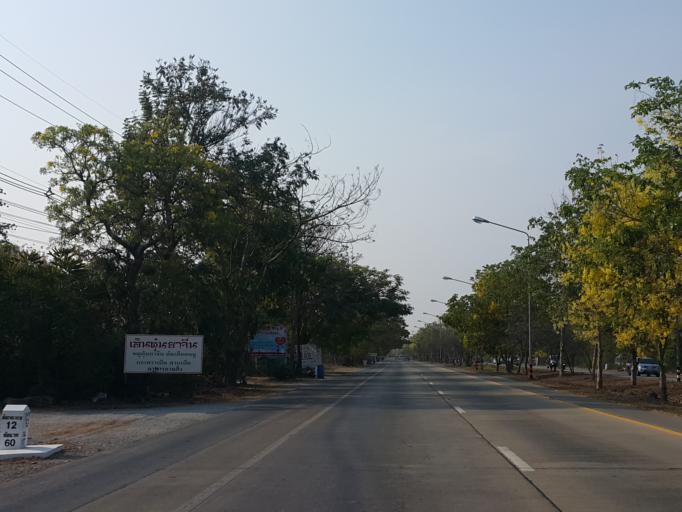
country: TH
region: Suphan Buri
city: Sam Chuk
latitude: 14.7759
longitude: 100.0903
